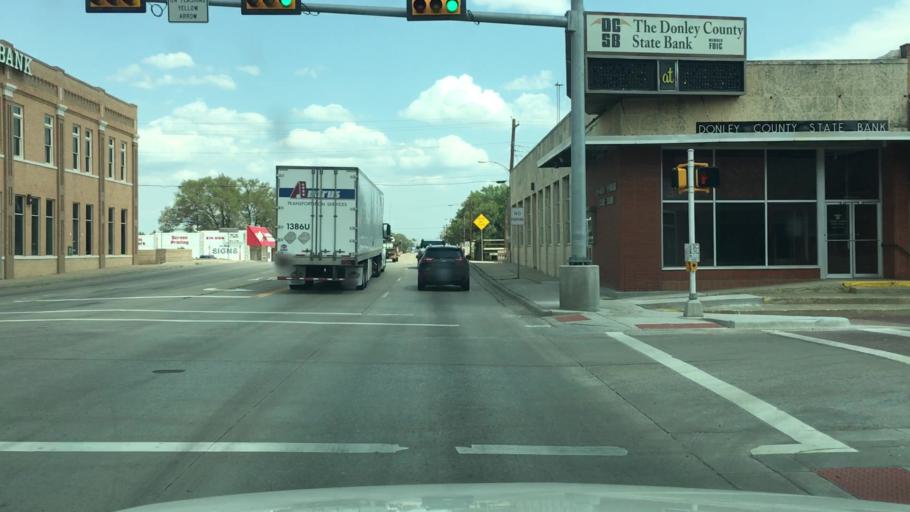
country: US
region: Texas
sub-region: Donley County
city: Clarendon
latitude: 34.9380
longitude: -100.8883
